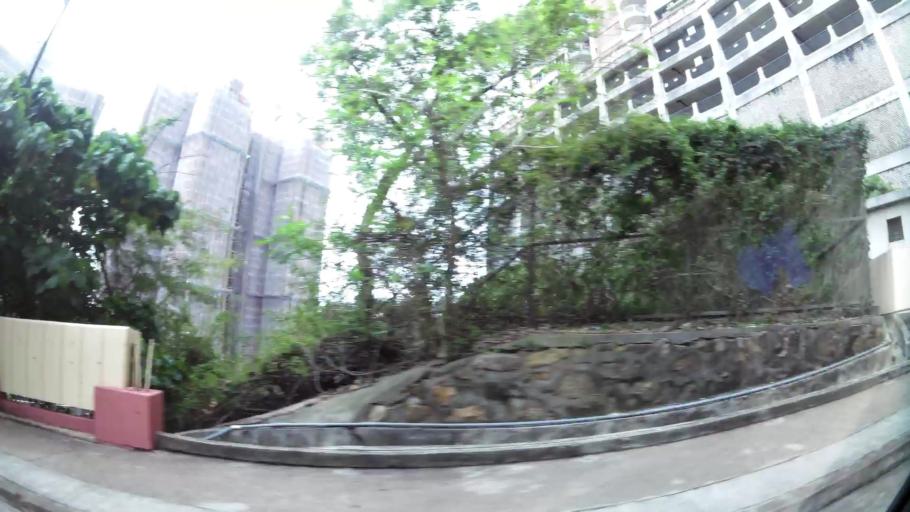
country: HK
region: Central and Western
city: Central
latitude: 22.2627
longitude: 114.1330
